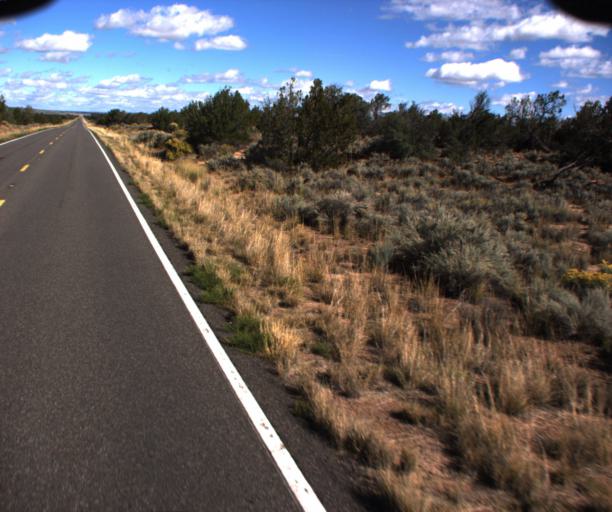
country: US
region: Arizona
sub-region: Apache County
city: Saint Johns
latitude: 34.8583
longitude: -109.2377
